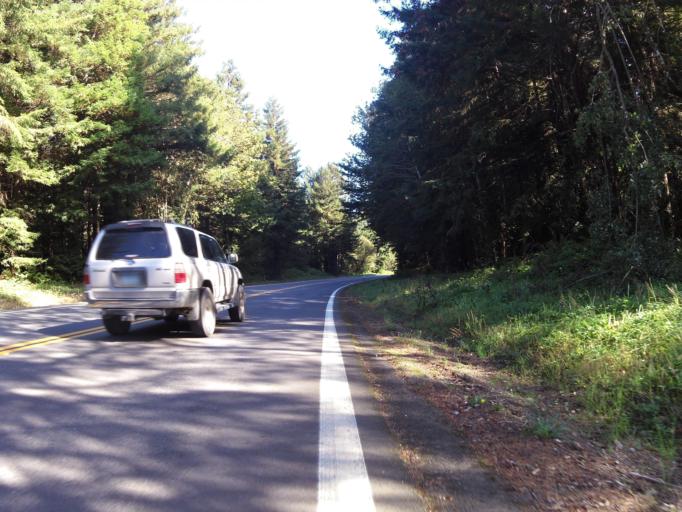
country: US
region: California
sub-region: Del Norte County
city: Bertsch-Oceanview
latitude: 41.8410
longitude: -124.1095
